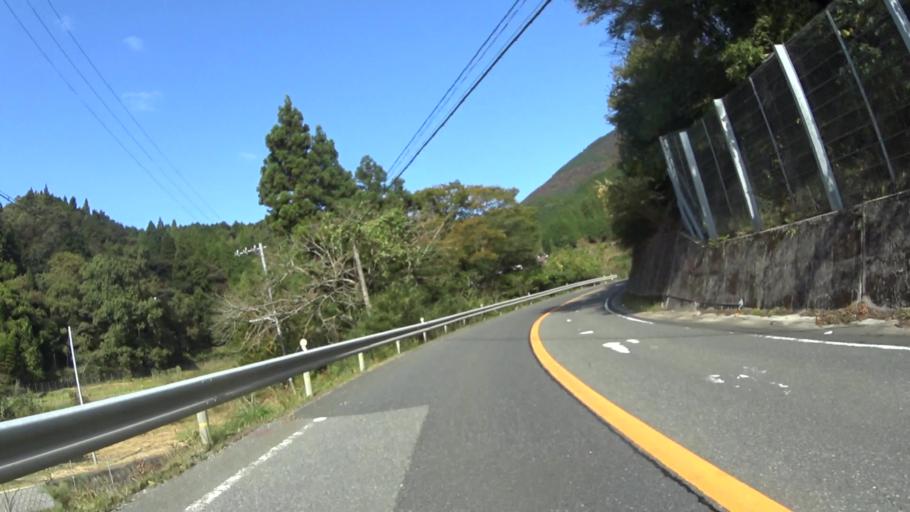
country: JP
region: Kyoto
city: Fukuchiyama
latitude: 35.3789
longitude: 135.0442
